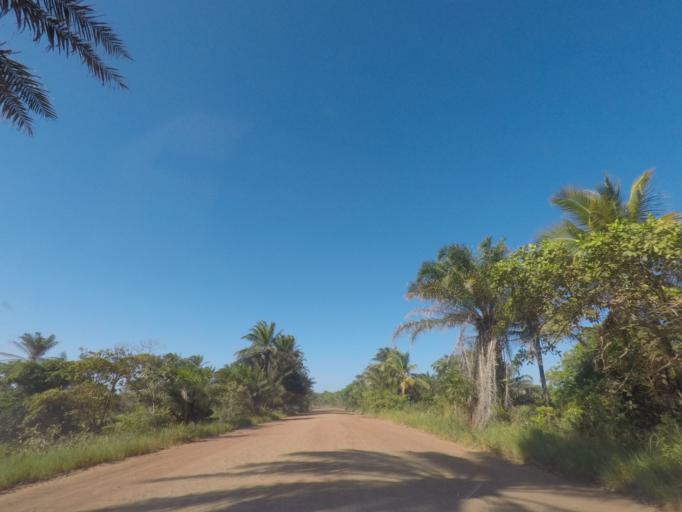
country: BR
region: Bahia
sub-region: Marau
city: Marau
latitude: -14.0522
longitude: -38.9550
